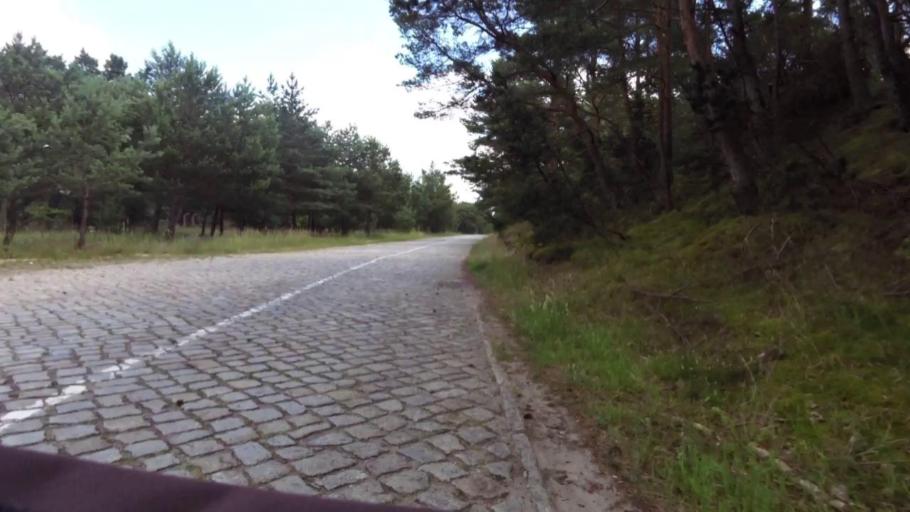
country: PL
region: West Pomeranian Voivodeship
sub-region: Powiat gryficki
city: Mrzezyno
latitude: 54.1269
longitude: 15.2179
